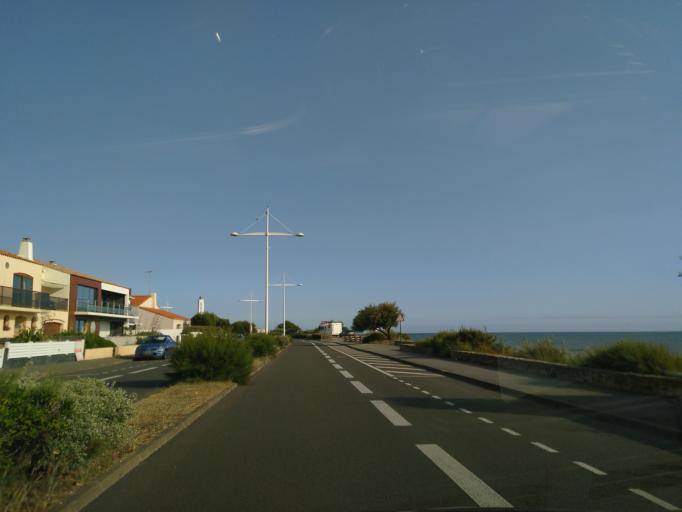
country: FR
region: Pays de la Loire
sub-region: Departement de la Vendee
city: Les Sables-d'Olonne
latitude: 46.4930
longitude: -1.8101
